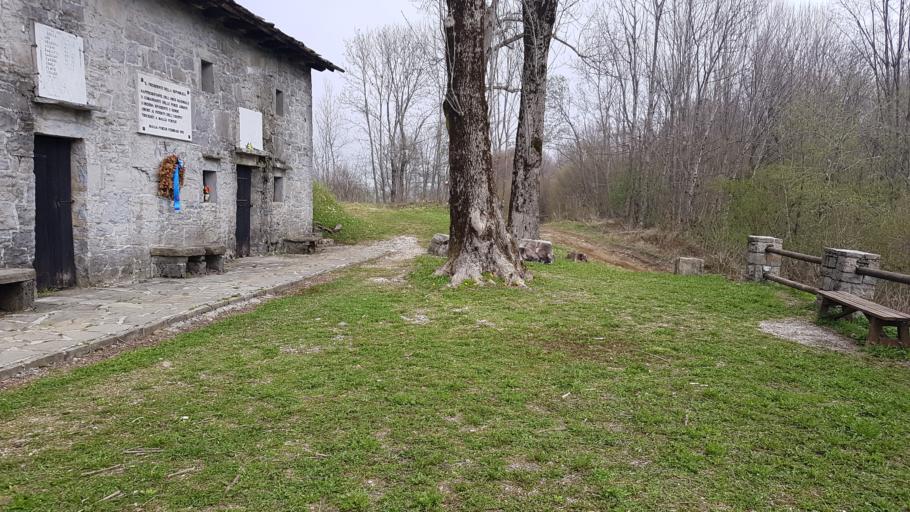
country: IT
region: Friuli Venezia Giulia
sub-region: Provincia di Udine
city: Faedis
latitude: 46.1900
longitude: 13.3834
